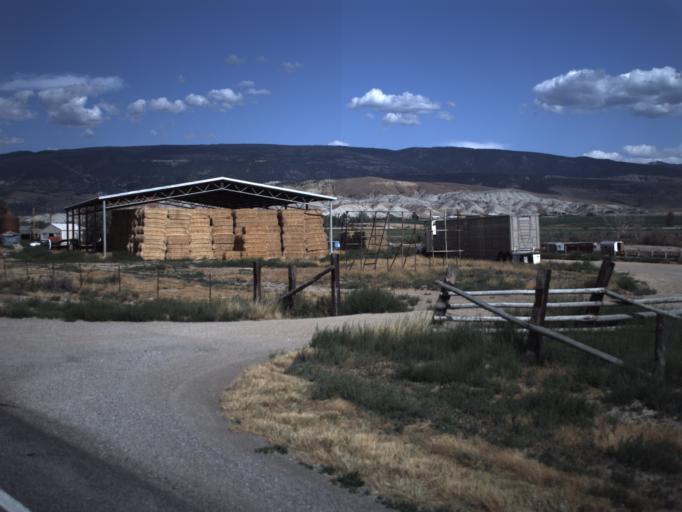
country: US
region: Utah
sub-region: Sanpete County
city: Gunnison
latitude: 39.1568
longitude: -111.7606
